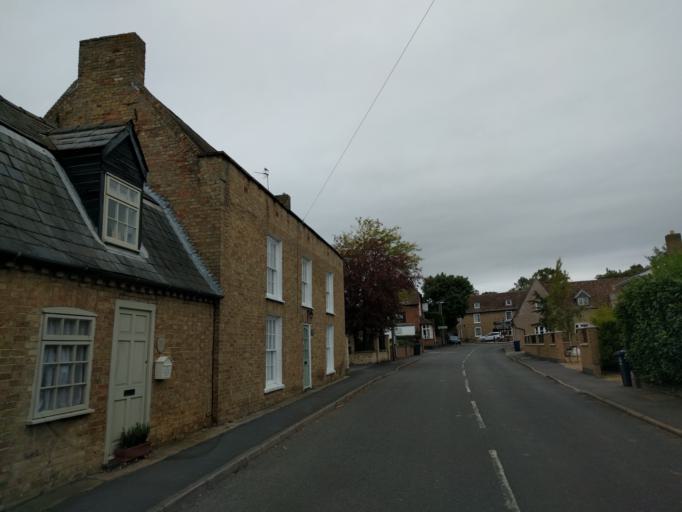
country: GB
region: England
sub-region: Cambridgeshire
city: Earith
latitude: 52.3533
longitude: 0.0069
